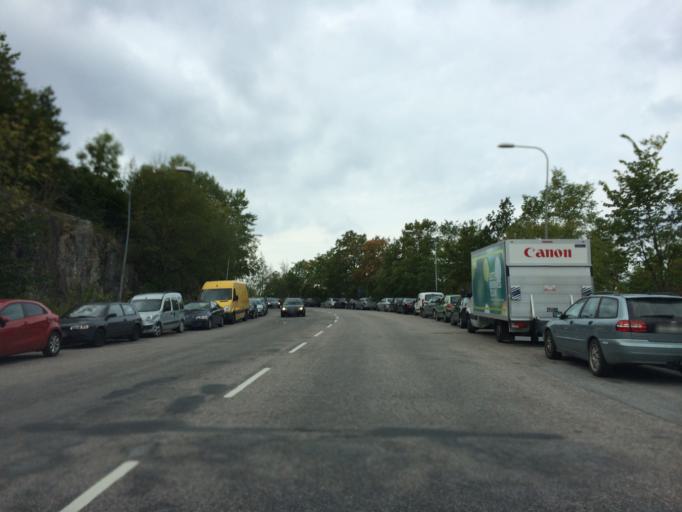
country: SE
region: Stockholm
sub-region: Stockholms Kommun
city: Arsta
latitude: 59.3092
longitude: 18.0191
